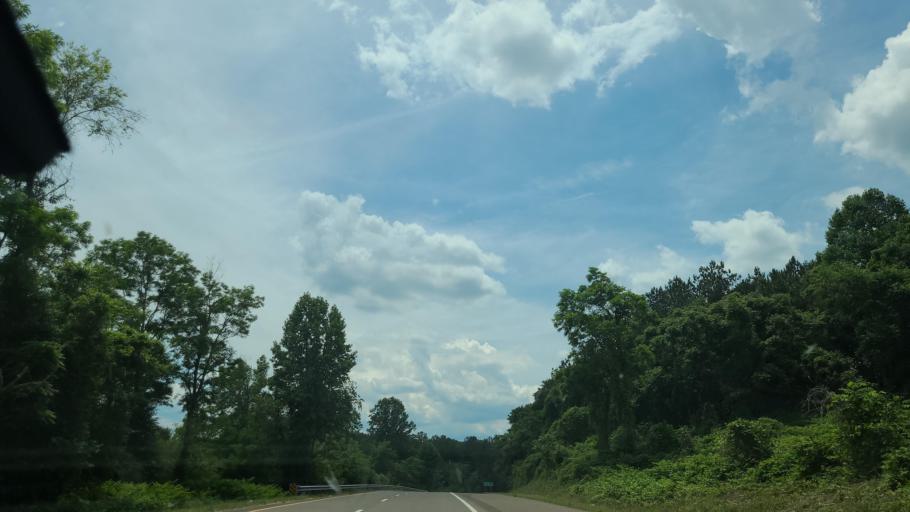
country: US
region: Georgia
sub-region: Fannin County
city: McCaysville
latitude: 35.0234
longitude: -84.3411
